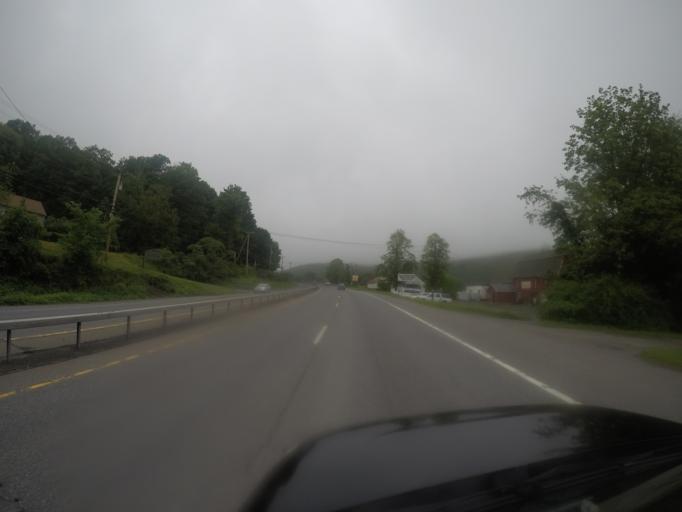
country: US
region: New York
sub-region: Ulster County
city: Hurley
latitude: 41.9553
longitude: -74.0490
